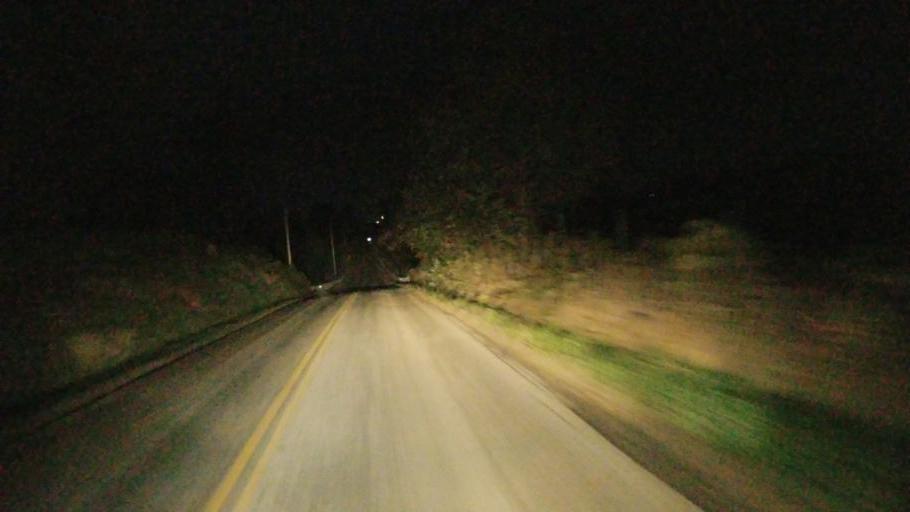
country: US
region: Ohio
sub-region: Wayne County
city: Apple Creek
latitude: 40.6690
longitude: -81.7459
